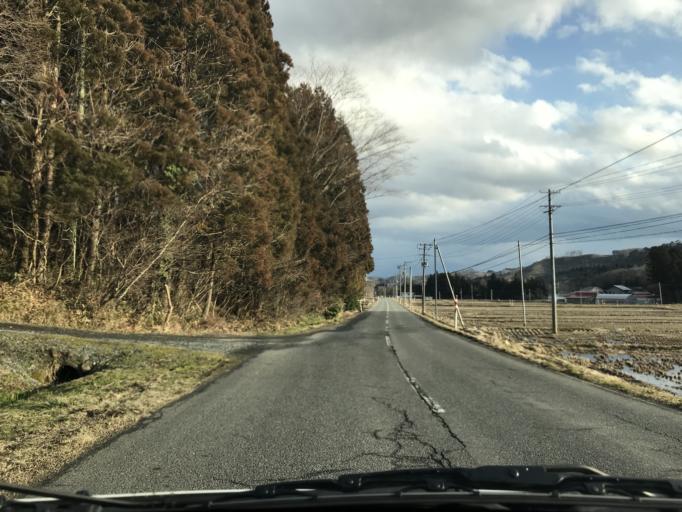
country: JP
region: Iwate
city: Mizusawa
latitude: 39.0600
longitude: 141.0363
